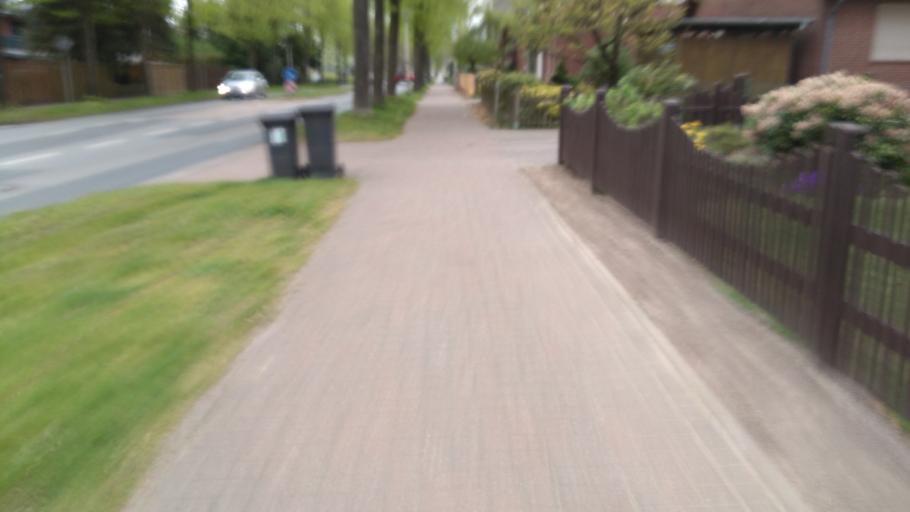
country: DE
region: Lower Saxony
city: Apensen
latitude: 53.4405
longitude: 9.6272
